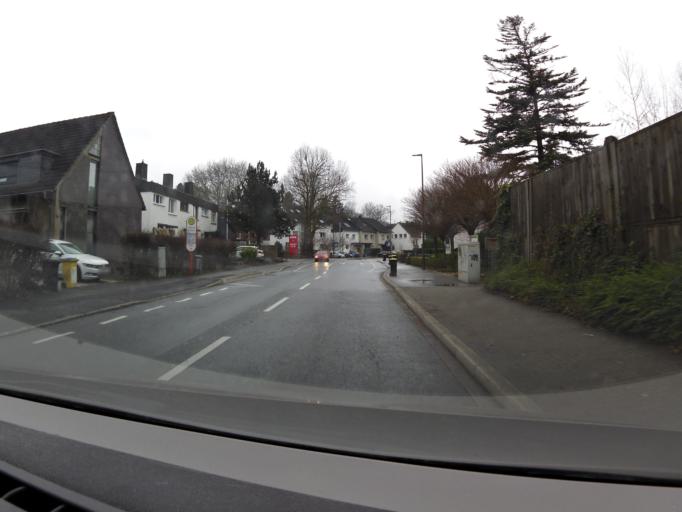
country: DE
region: North Rhine-Westphalia
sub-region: Regierungsbezirk Arnsberg
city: Dortmund
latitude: 51.4619
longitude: 7.4801
